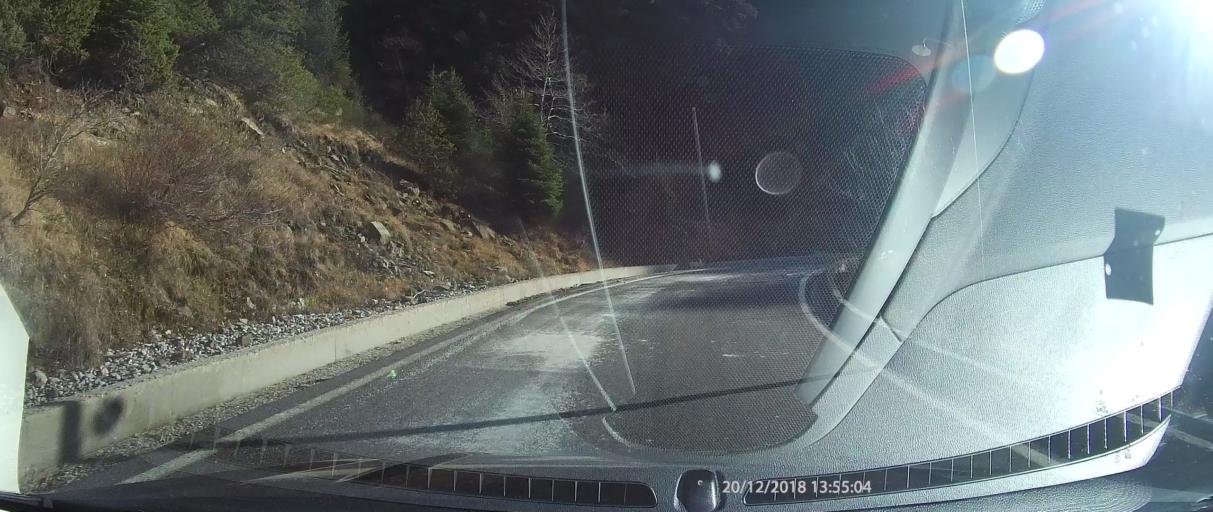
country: GR
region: West Greece
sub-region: Nomos Aitolias kai Akarnanias
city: Paravola
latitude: 38.7124
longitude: 21.6142
